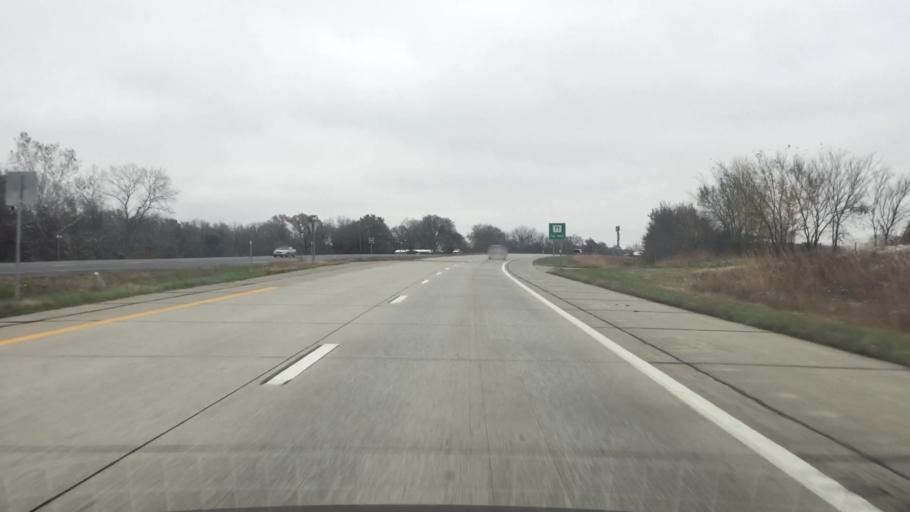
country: US
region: Missouri
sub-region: Saint Clair County
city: Osceola
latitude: 38.0136
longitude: -93.6605
